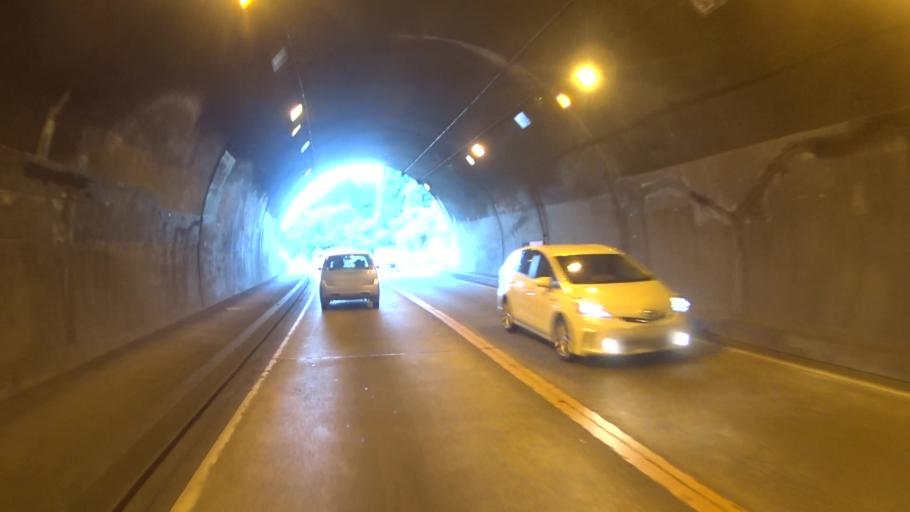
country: JP
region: Kyoto
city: Miyazu
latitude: 35.5505
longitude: 135.1721
